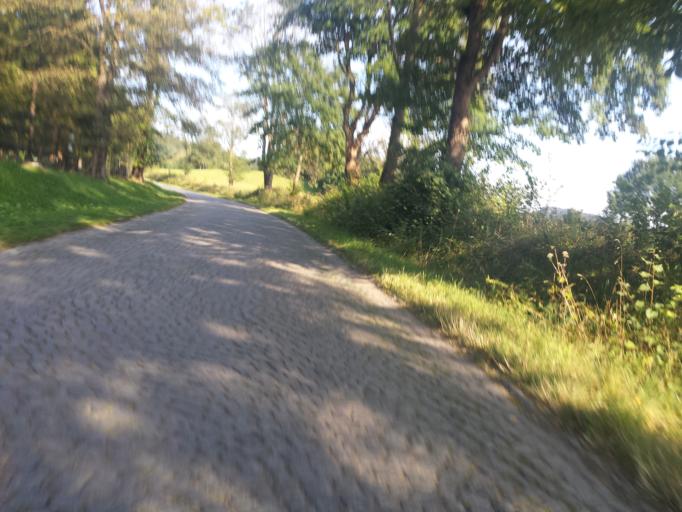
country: PL
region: Subcarpathian Voivodeship
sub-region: Powiat leski
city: Uherce Mineralne
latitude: 49.4447
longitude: 22.3969
